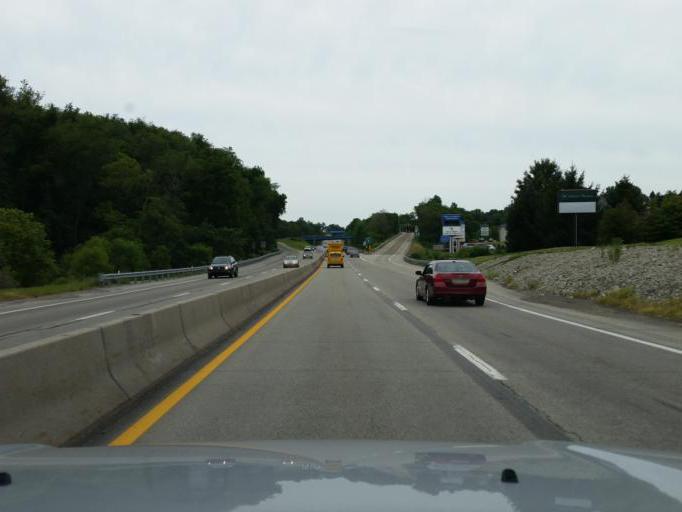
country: US
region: Pennsylvania
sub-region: Westmoreland County
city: Greensburg
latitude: 40.2930
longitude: -79.5245
